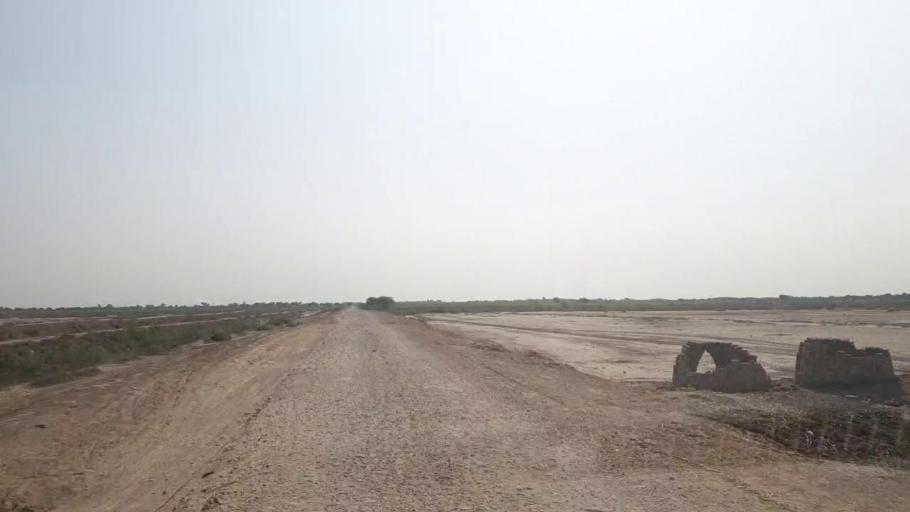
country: PK
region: Sindh
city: Kadhan
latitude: 24.4738
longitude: 68.9031
